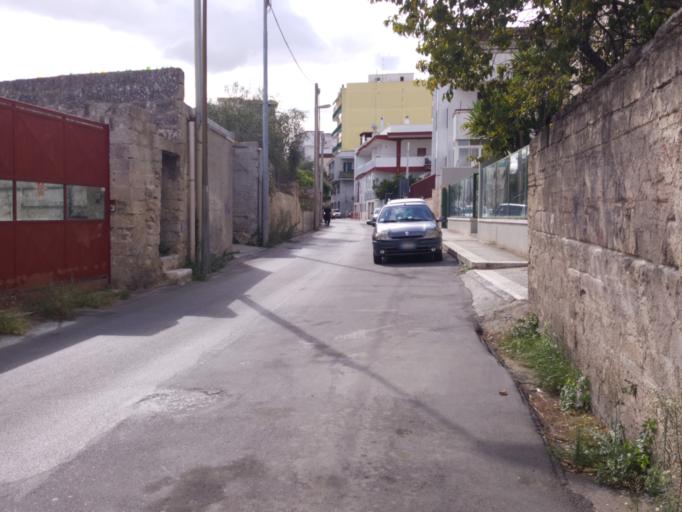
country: IT
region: Apulia
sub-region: Provincia di Bari
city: Triggiano
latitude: 41.0673
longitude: 16.9200
